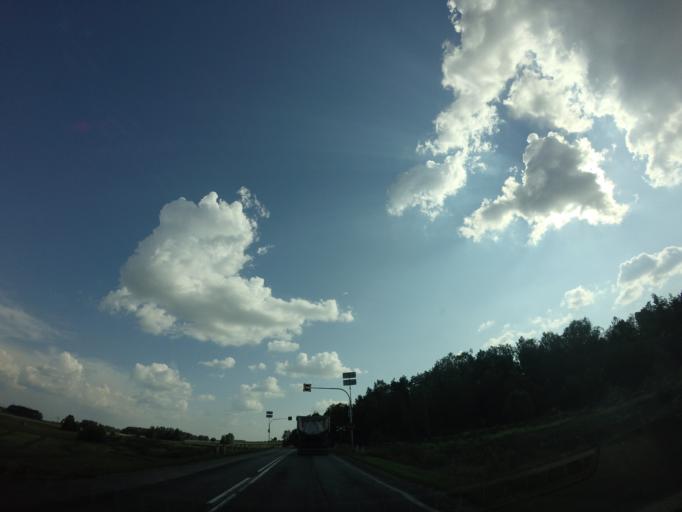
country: PL
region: Masovian Voivodeship
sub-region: Powiat sokolowski
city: Bielany
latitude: 52.3294
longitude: 22.2399
